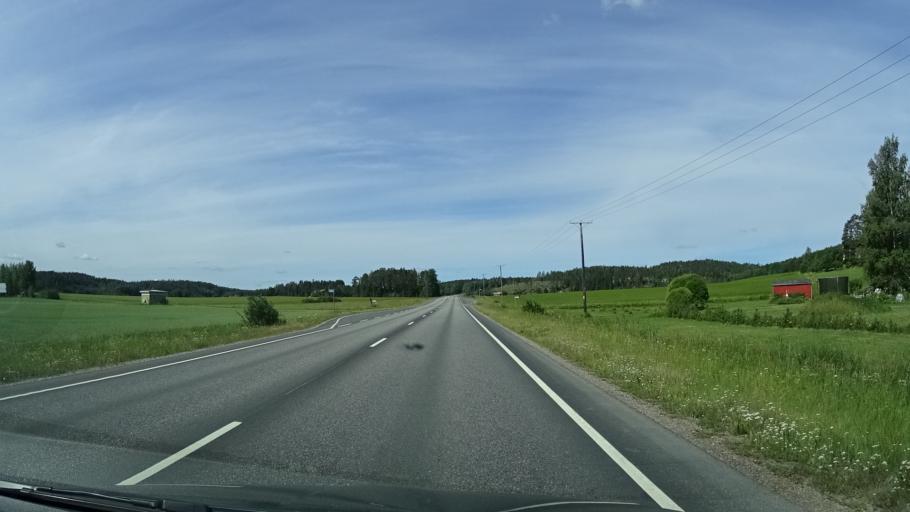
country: FI
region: Varsinais-Suomi
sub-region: Salo
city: Muurla
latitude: 60.3828
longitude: 23.2709
